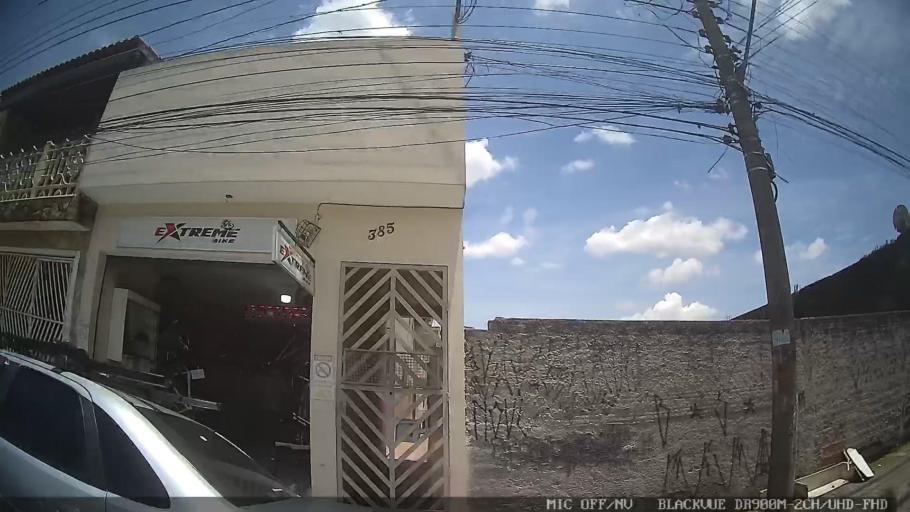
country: BR
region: Sao Paulo
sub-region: Suzano
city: Suzano
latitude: -23.5304
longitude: -46.3076
